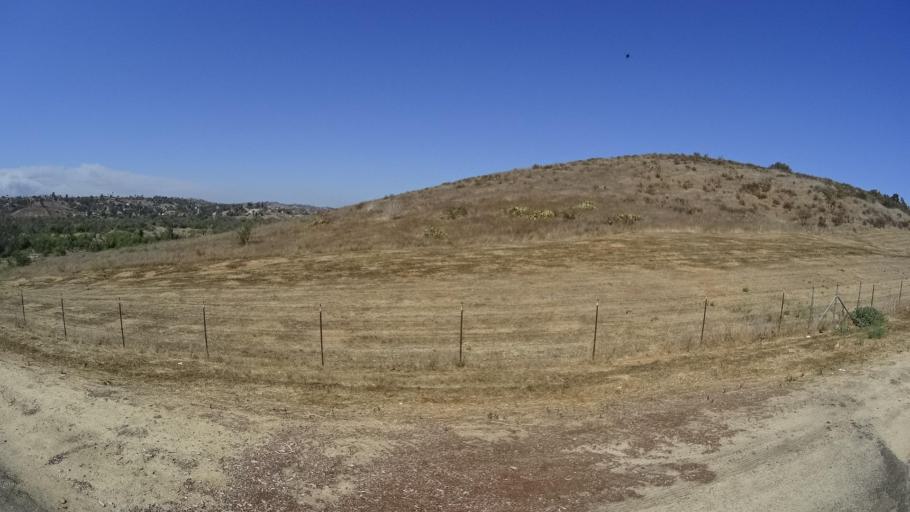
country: US
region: California
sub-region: San Diego County
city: Bonsall
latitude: 33.2978
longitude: -117.2085
